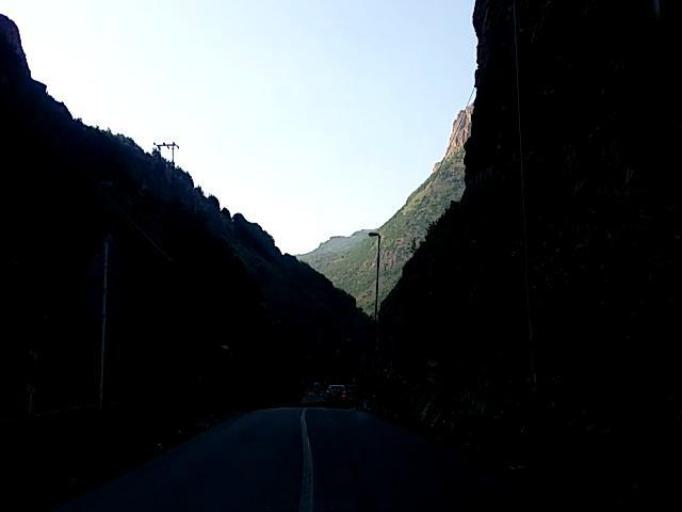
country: IR
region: Tehran
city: Tajrish
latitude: 36.2044
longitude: 51.3299
